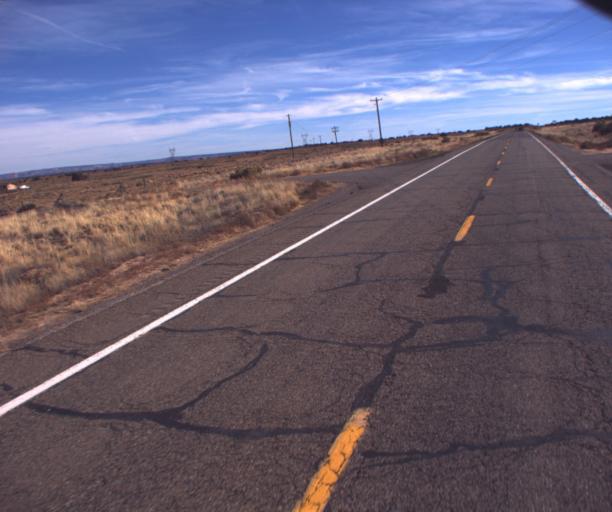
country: US
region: Arizona
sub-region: Coconino County
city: Kaibito
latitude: 36.6163
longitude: -110.9468
